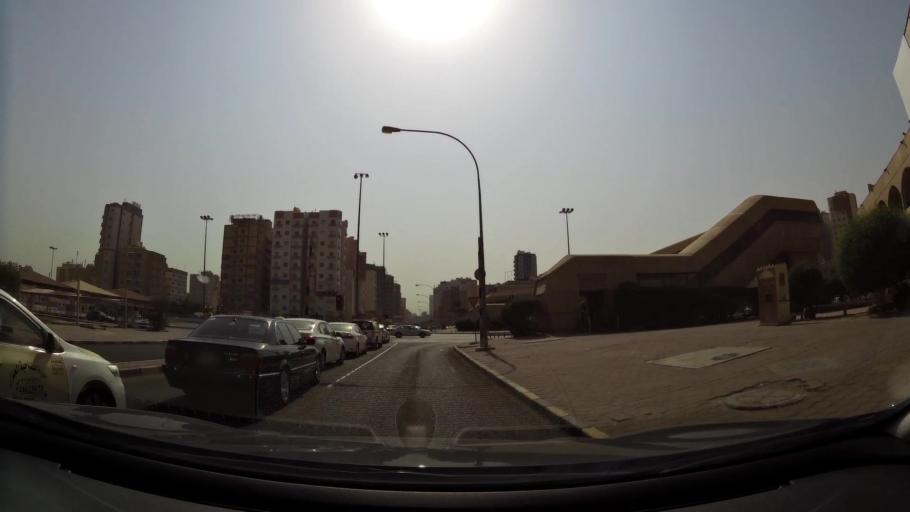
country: KW
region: Muhafazat Hawalli
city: Hawalli
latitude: 29.3328
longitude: 48.0091
